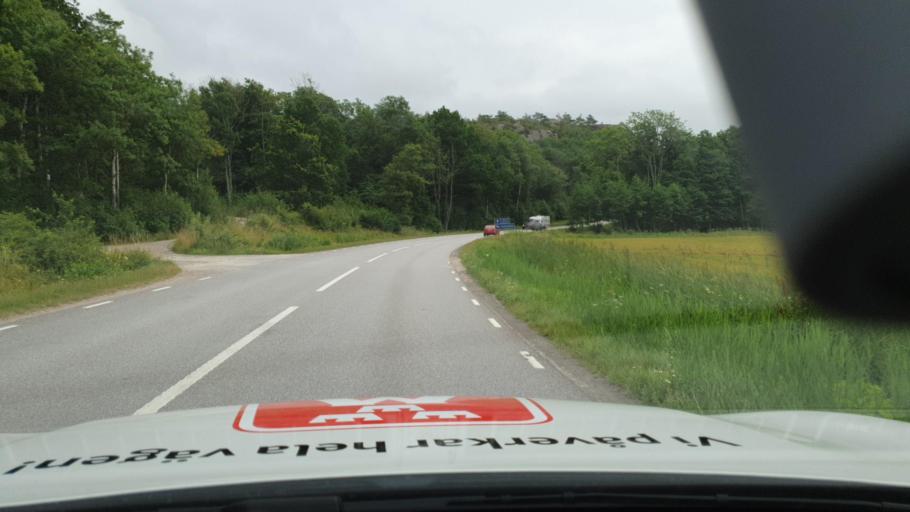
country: SE
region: Vaestra Goetaland
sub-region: Sotenas Kommun
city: Hunnebostrand
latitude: 58.4654
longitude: 11.3374
